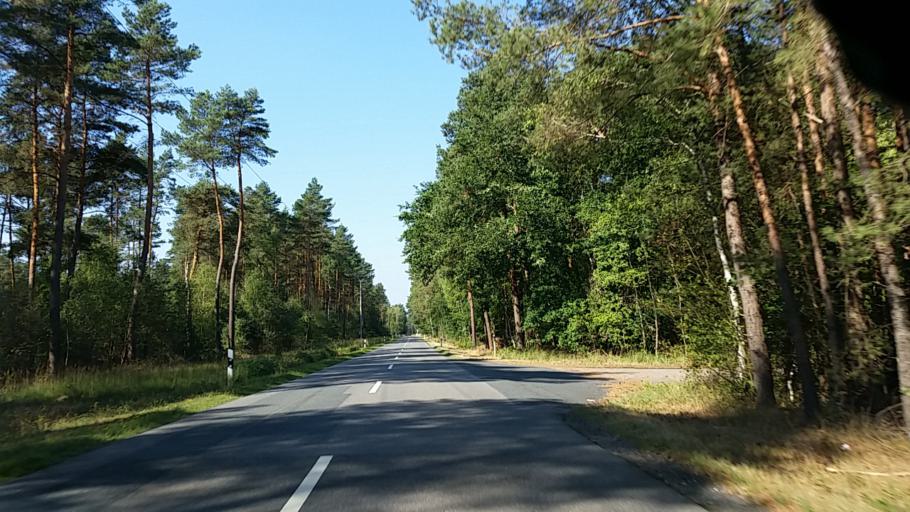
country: DE
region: Lower Saxony
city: Steinhorst
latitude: 52.6693
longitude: 10.4223
